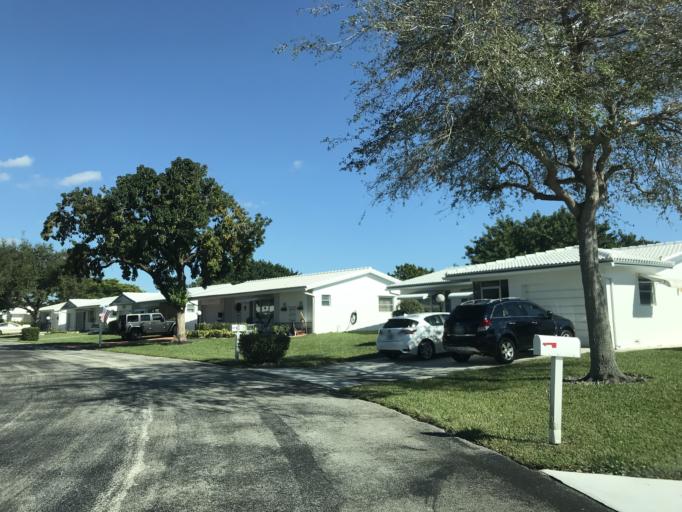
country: US
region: Florida
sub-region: Broward County
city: Plantation
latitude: 26.1389
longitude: -80.2676
